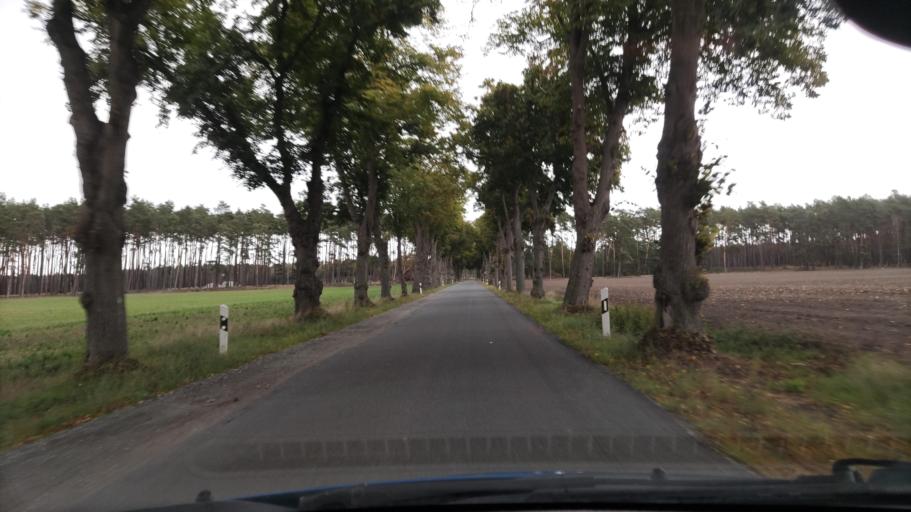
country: DE
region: Saxony-Anhalt
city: Luftkurort Arendsee
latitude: 52.9480
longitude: 11.5400
